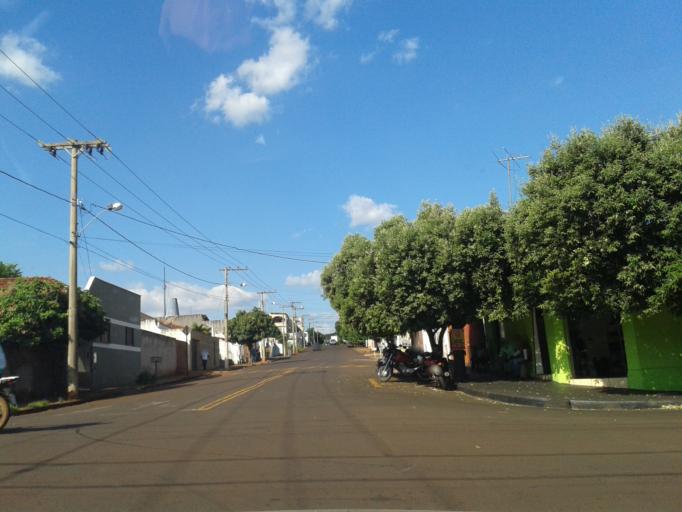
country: BR
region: Minas Gerais
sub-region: Ituiutaba
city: Ituiutaba
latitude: -18.9697
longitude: -49.4560
